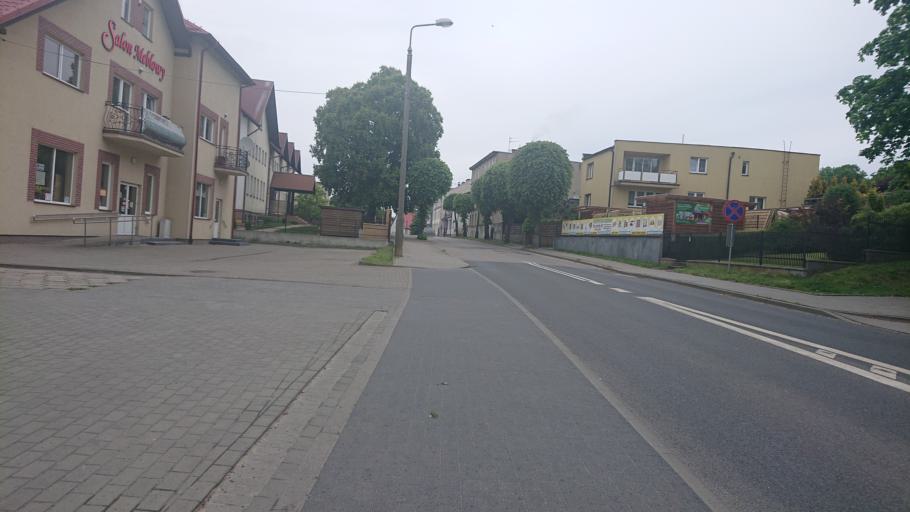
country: PL
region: Pomeranian Voivodeship
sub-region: Powiat chojnicki
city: Chojnice
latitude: 53.6953
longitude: 17.5667
